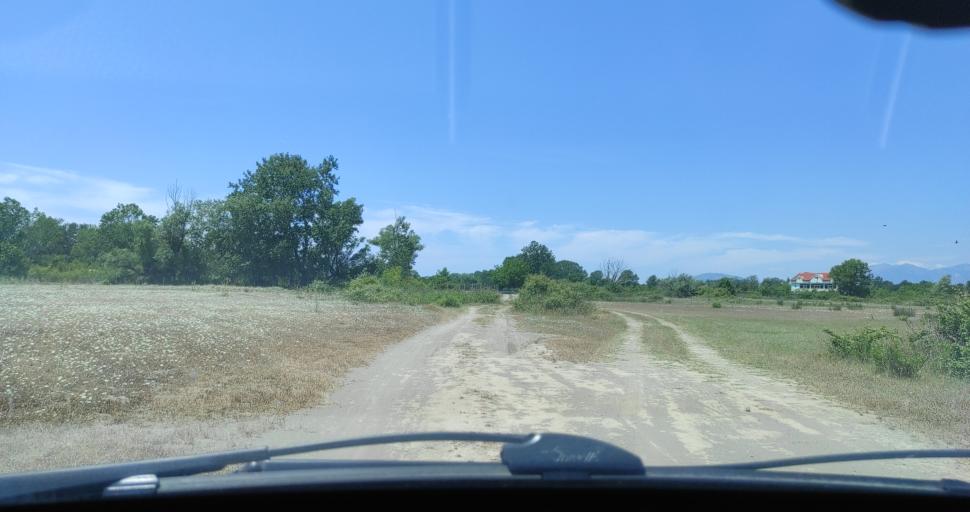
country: AL
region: Shkoder
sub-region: Rrethi i Shkodres
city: Velipoje
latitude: 41.8698
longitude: 19.3959
